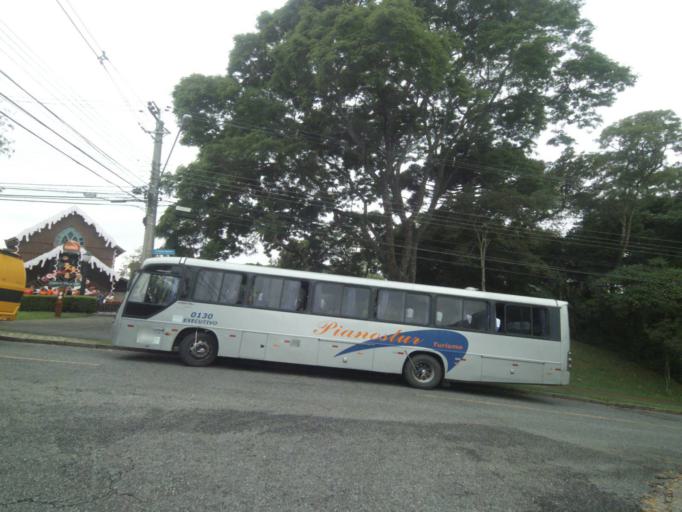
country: BR
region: Parana
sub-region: Curitiba
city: Curitiba
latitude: -25.4048
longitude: -49.2882
